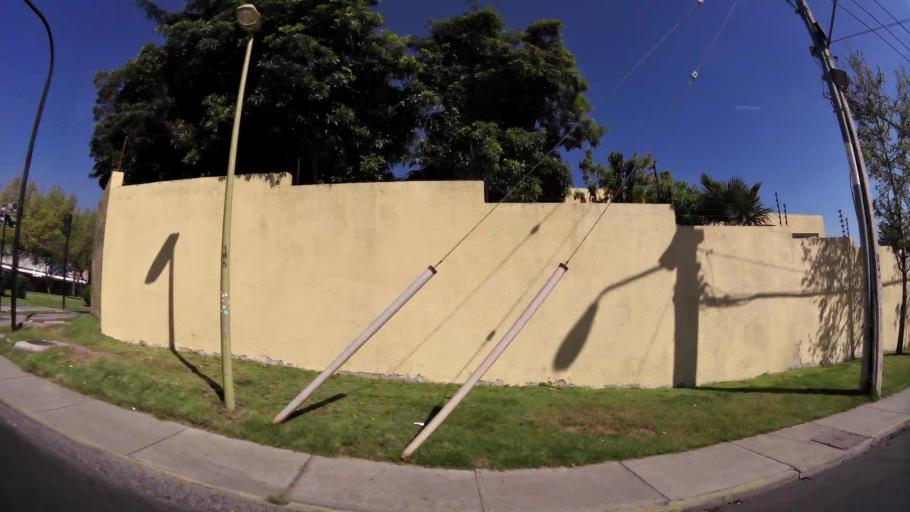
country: CL
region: Santiago Metropolitan
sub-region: Provincia de Santiago
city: Villa Presidente Frei, Nunoa, Santiago, Chile
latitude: -33.4014
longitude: -70.5176
